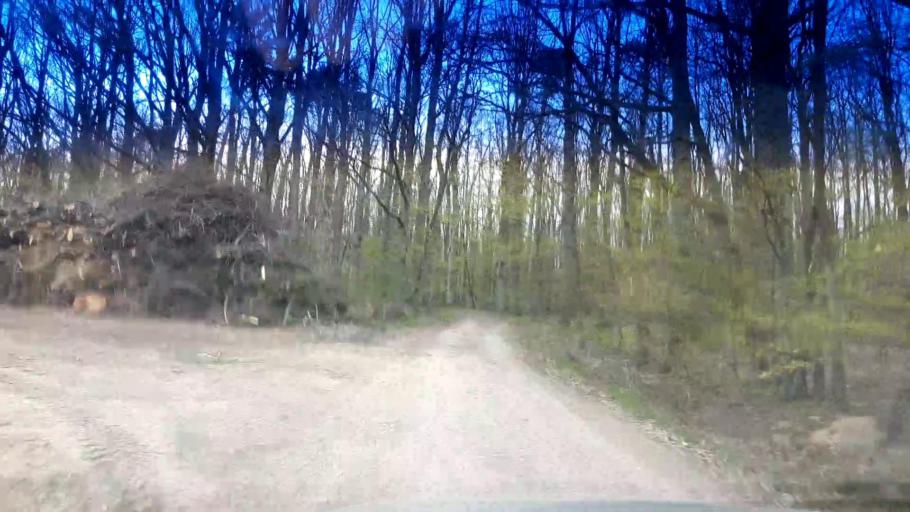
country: DE
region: Bavaria
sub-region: Upper Franconia
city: Schesslitz
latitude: 50.0001
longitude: 11.0321
